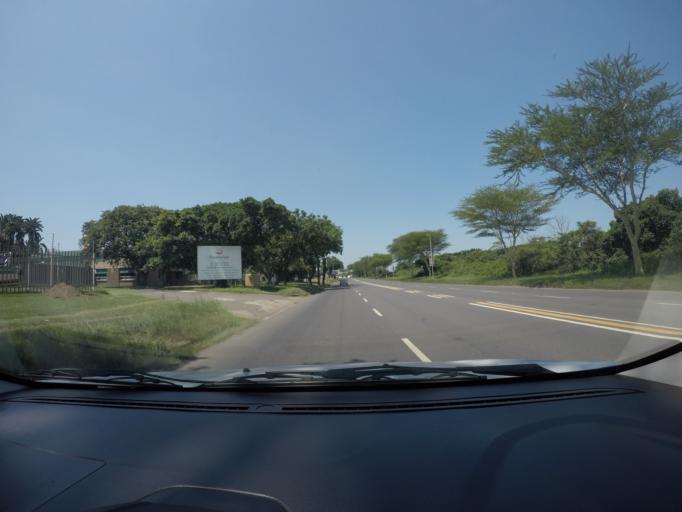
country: ZA
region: KwaZulu-Natal
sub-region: uThungulu District Municipality
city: Richards Bay
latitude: -28.7658
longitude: 32.0183
